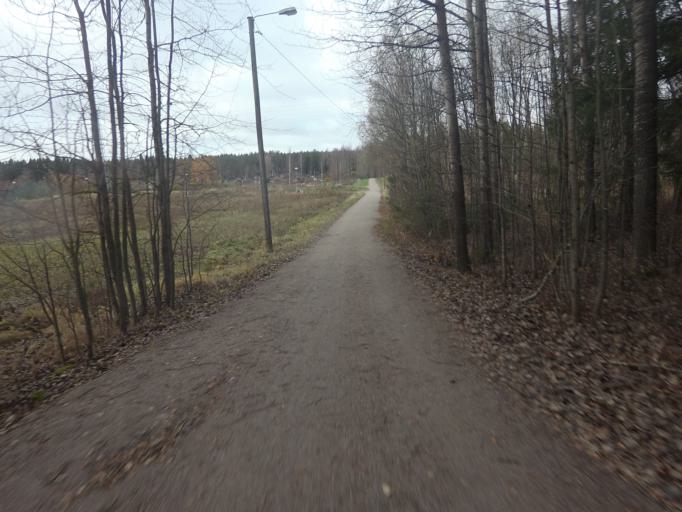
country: FI
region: Uusimaa
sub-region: Helsinki
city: Kauniainen
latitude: 60.1789
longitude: 24.7090
